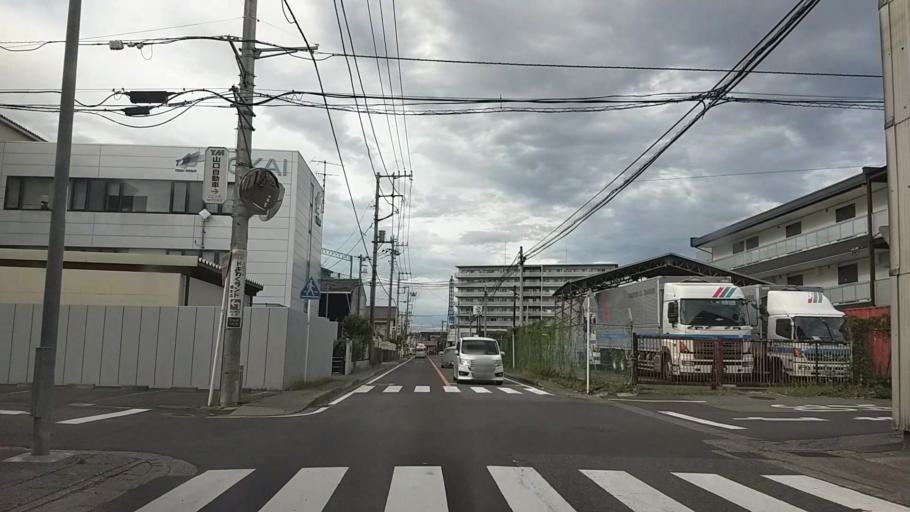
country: JP
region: Tokyo
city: Hachioji
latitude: 35.5802
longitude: 139.3420
